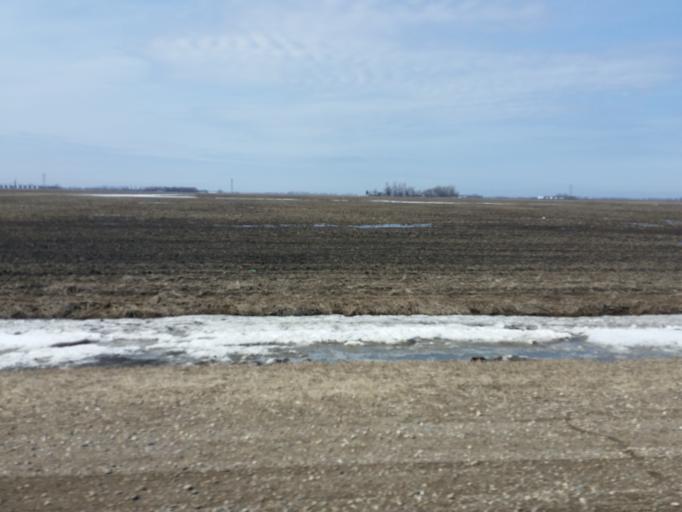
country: US
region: North Dakota
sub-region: Walsh County
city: Grafton
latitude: 48.3007
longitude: -97.2549
